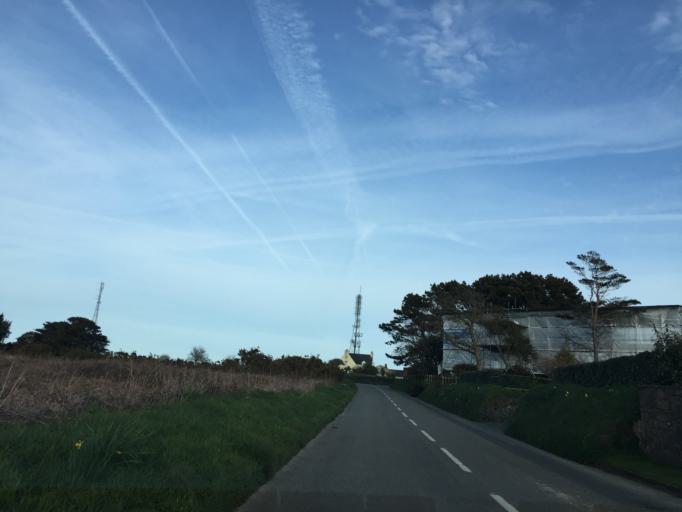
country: JE
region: St Helier
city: Saint Helier
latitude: 49.2463
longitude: -2.1060
